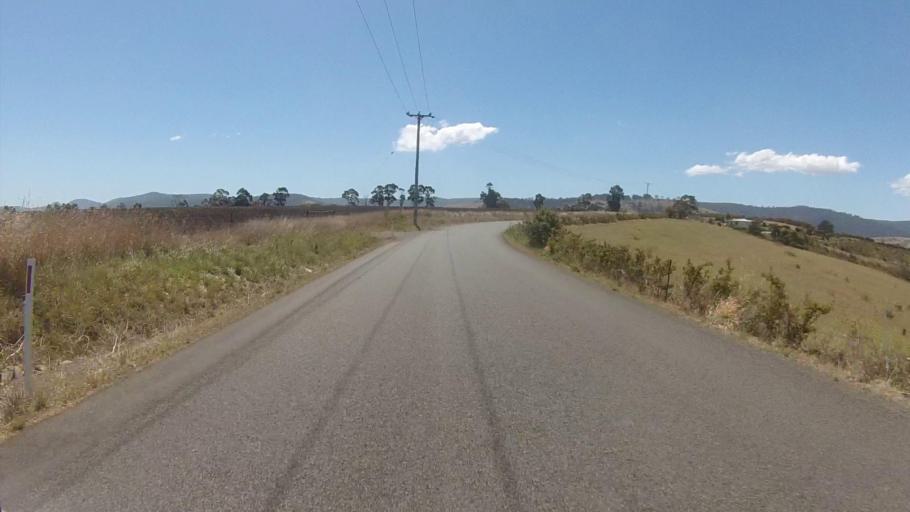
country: AU
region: Tasmania
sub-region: Sorell
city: Sorell
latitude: -42.7760
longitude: 147.5807
